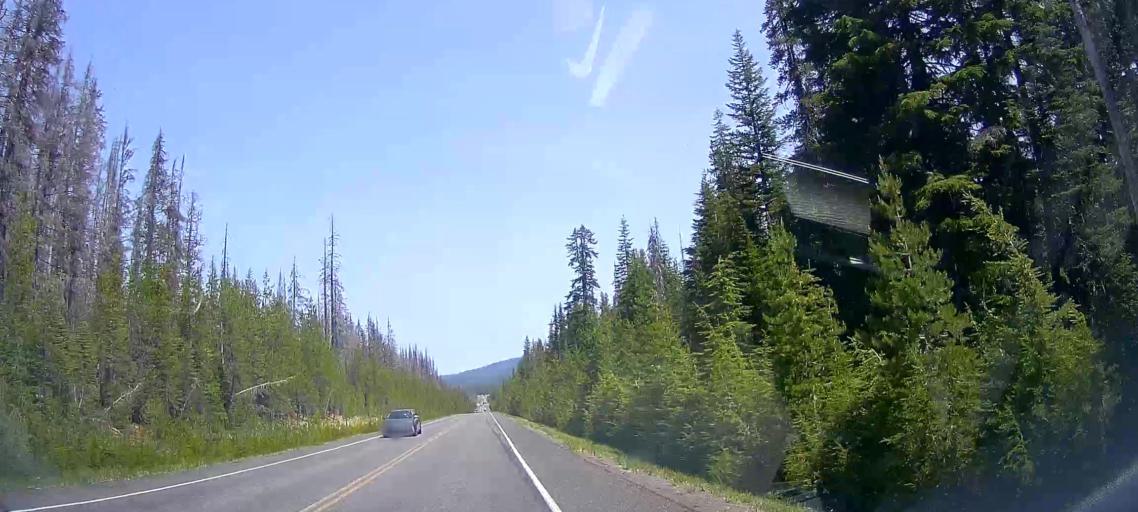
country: US
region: Oregon
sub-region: Lane County
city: Oakridge
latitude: 43.0698
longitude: -122.1193
